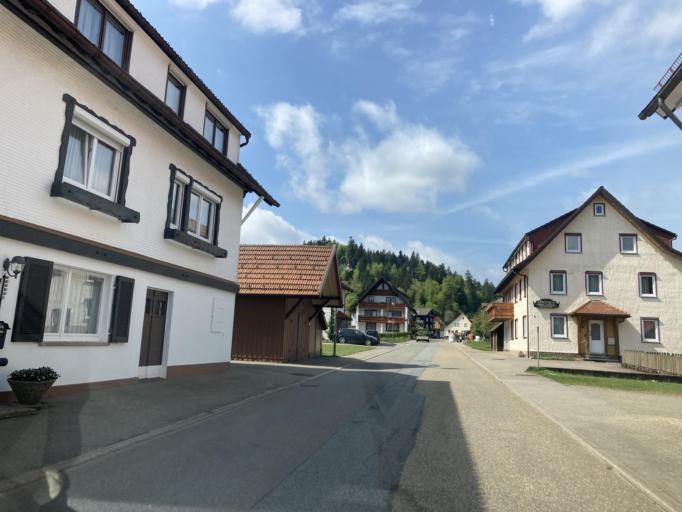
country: DE
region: Baden-Wuerttemberg
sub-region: Karlsruhe Region
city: Biberach
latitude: 48.5288
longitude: 8.2772
